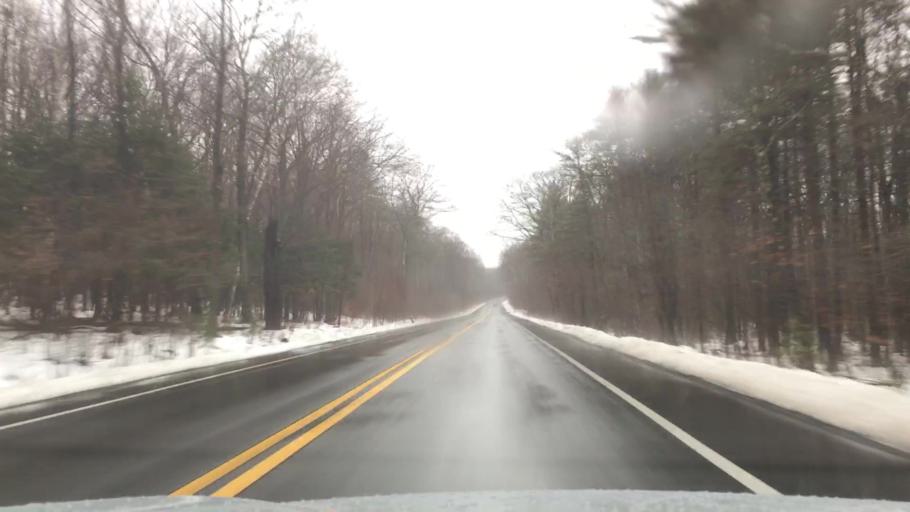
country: US
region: Massachusetts
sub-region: Hampshire County
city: Pelham
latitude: 42.4058
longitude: -72.4031
